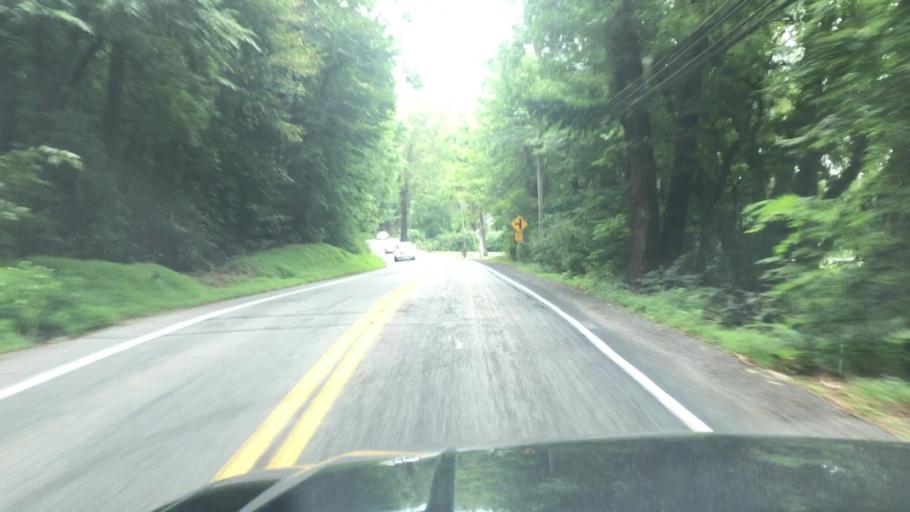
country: US
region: Pennsylvania
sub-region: Cumberland County
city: Shiremanstown
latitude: 40.2598
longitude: -76.9765
